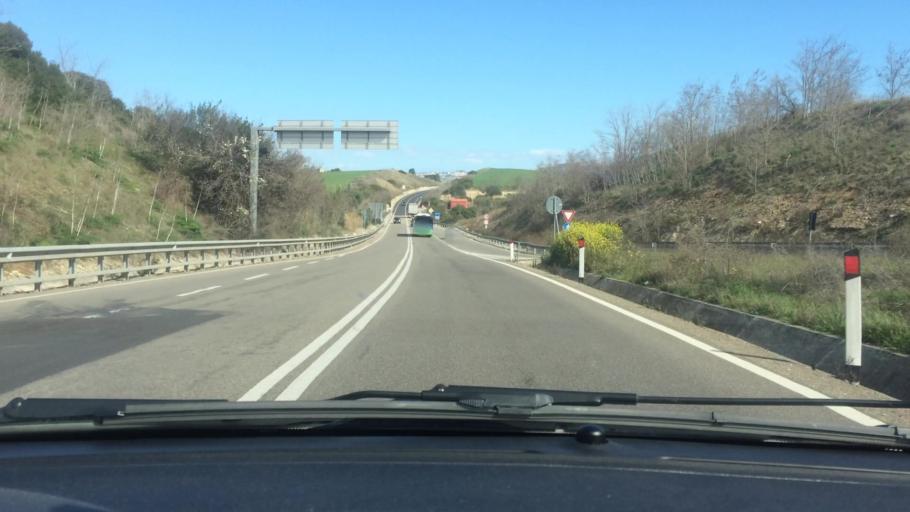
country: IT
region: Basilicate
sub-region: Provincia di Matera
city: Miglionico
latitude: 40.5967
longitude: 16.5657
